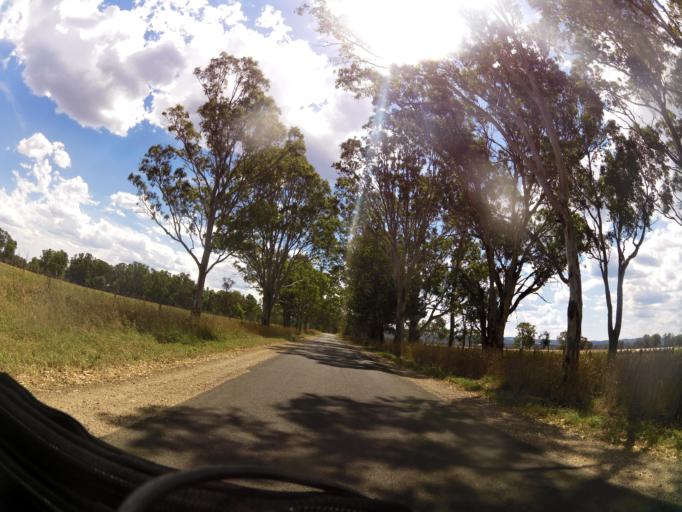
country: AU
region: Victoria
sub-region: Wellington
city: Heyfield
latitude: -37.9831
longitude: 146.7148
